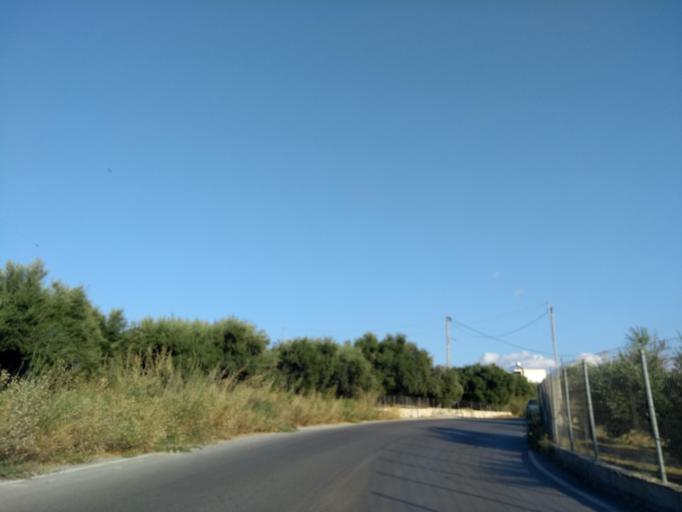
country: GR
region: Crete
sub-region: Nomos Chanias
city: Kalivai
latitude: 35.4444
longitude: 24.1758
